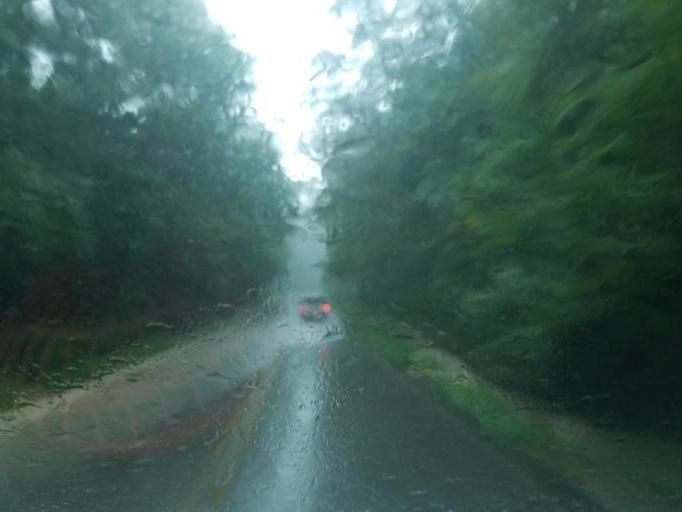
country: US
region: Kentucky
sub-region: Carter County
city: Olive Hill
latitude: 38.3515
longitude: -83.2028
